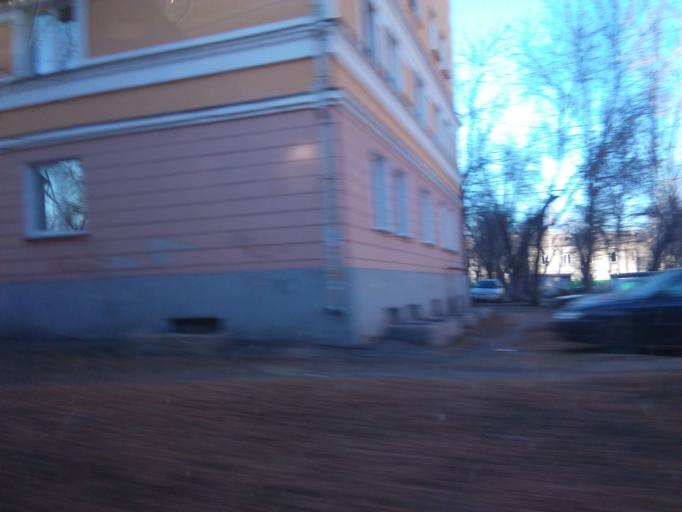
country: RU
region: Chelyabinsk
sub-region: Gorod Magnitogorsk
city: Magnitogorsk
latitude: 53.3886
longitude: 59.0672
